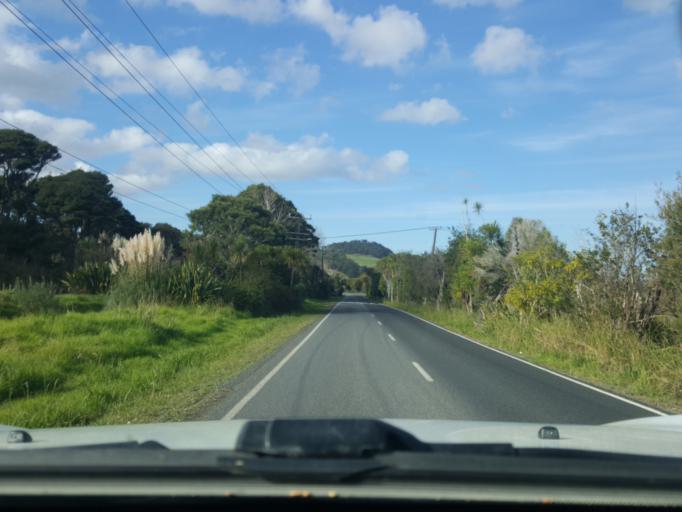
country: NZ
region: Auckland
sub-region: Auckland
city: Muriwai Beach
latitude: -36.7474
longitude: 174.4348
